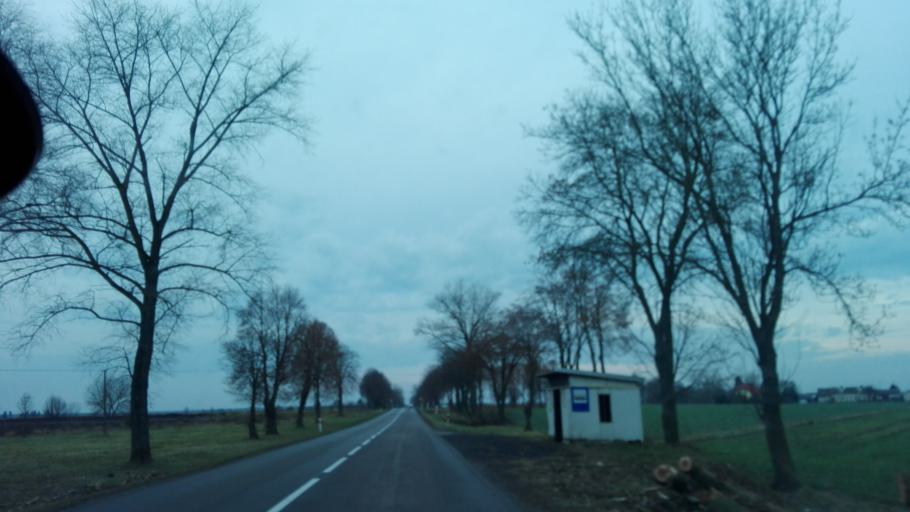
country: PL
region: Lublin Voivodeship
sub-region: Powiat radzynski
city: Wohyn
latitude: 51.7791
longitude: 22.7896
